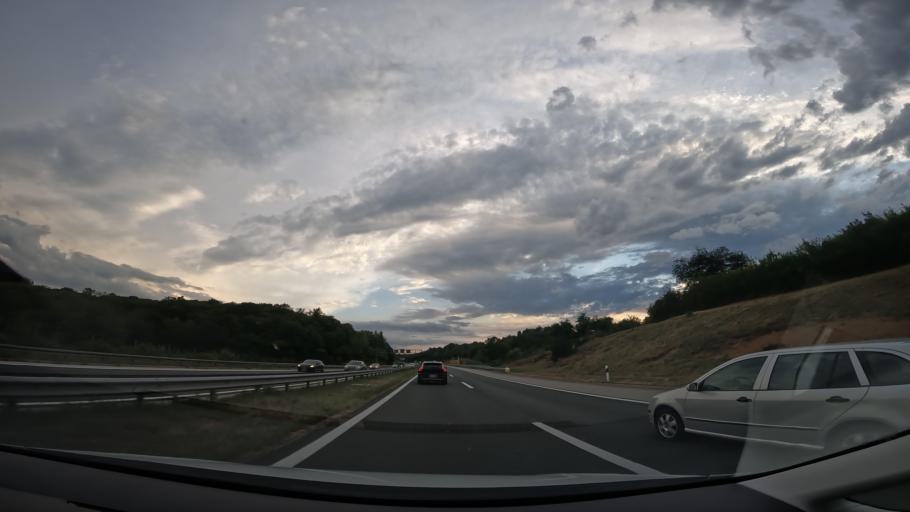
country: HR
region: Karlovacka
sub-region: Grad Karlovac
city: Karlovac
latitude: 45.4844
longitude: 15.4419
